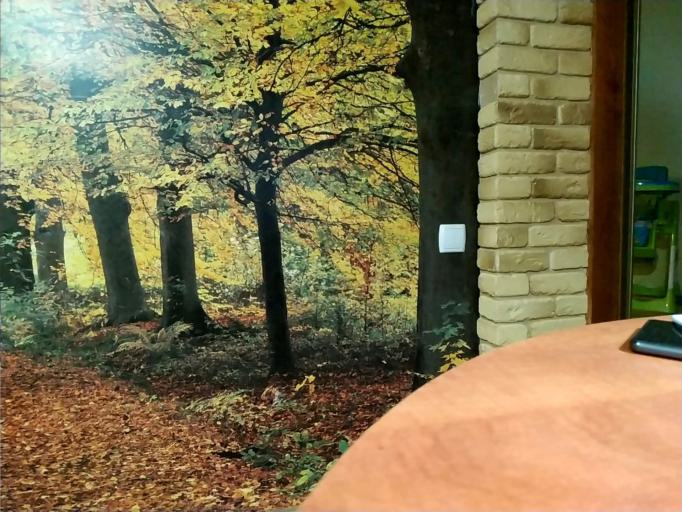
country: BY
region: Minsk
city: Plyeshchanitsy
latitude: 54.4283
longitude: 27.6312
